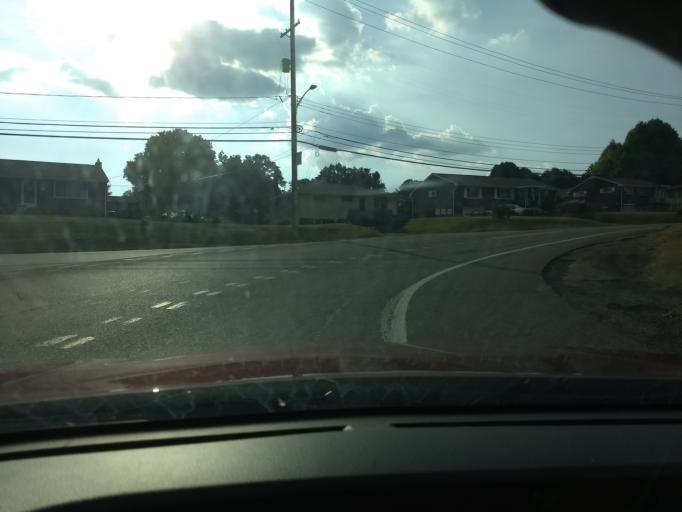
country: US
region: Pennsylvania
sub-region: Allegheny County
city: Curtisville
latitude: 40.6209
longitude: -79.8582
